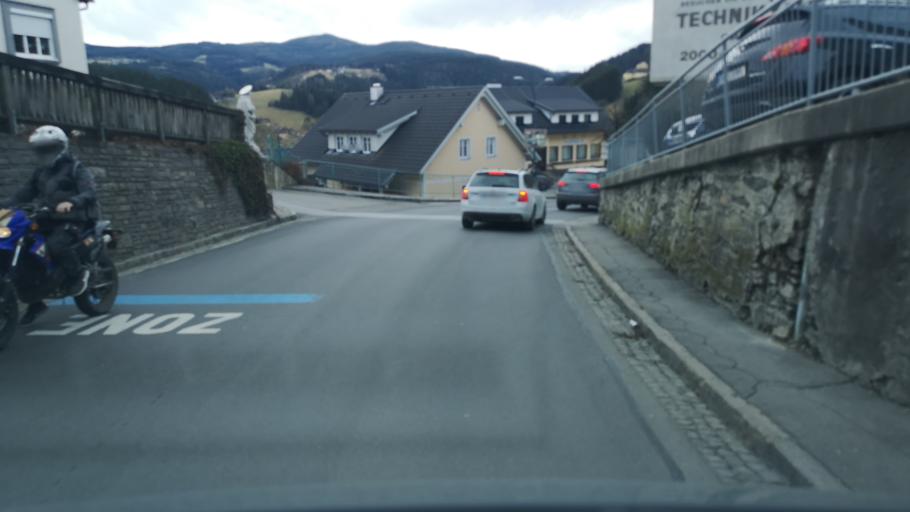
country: AT
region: Styria
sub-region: Politischer Bezirk Weiz
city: Birkfeld
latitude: 47.3544
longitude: 15.6948
